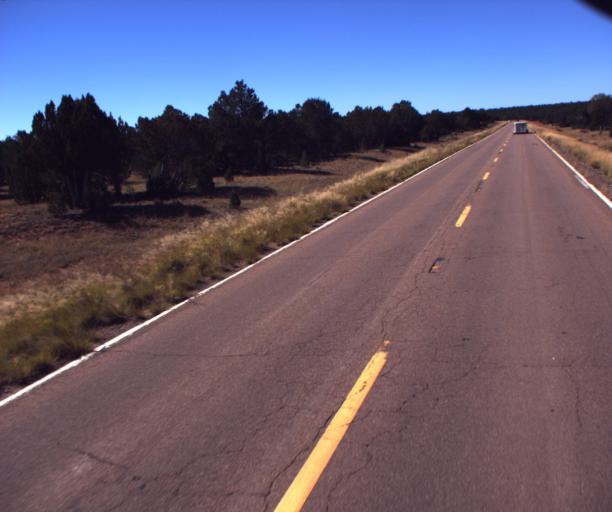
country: US
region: Arizona
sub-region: Navajo County
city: Heber-Overgaard
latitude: 34.4579
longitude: -110.5148
